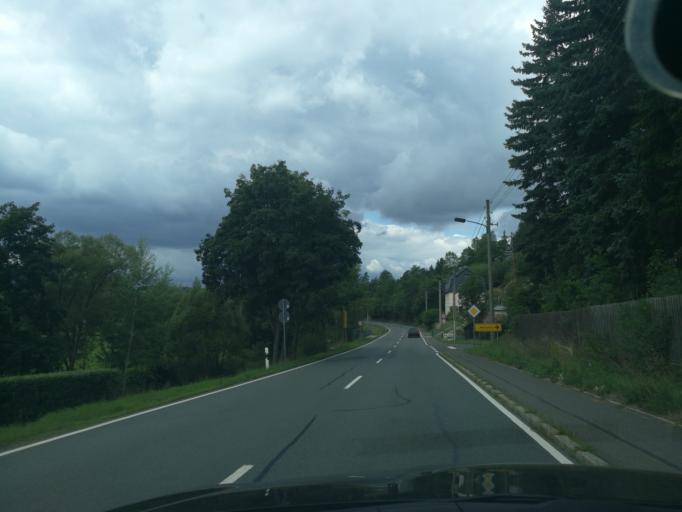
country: DE
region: Saxony
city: Eichigt
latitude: 50.3642
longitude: 12.2225
